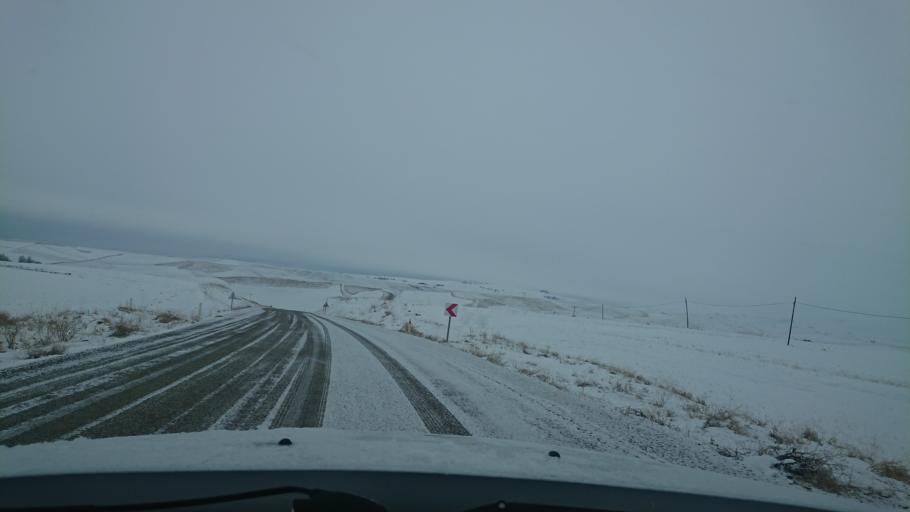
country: TR
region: Aksaray
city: Agacoren
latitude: 38.7815
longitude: 33.8714
